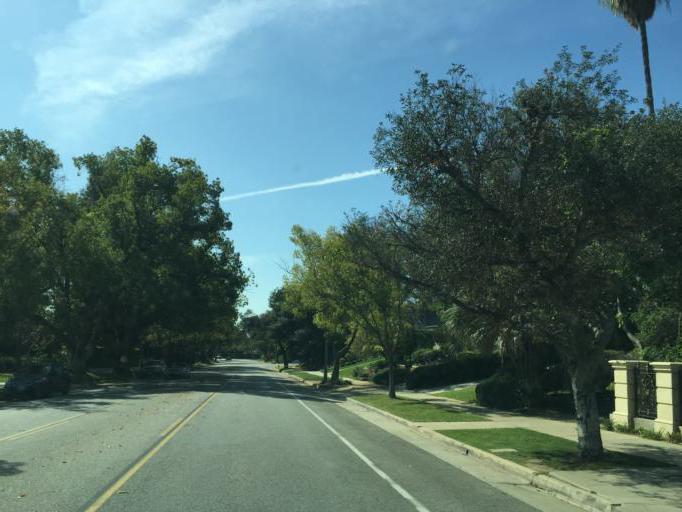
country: US
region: California
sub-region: Los Angeles County
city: South Pasadena
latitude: 34.1267
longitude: -118.1355
